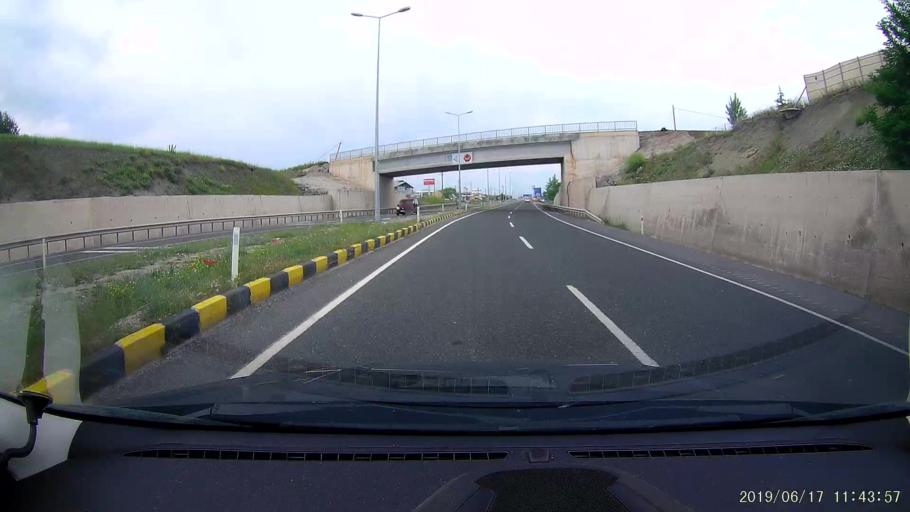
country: TR
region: Cankiri
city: Kursunlu
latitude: 40.8412
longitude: 33.2721
